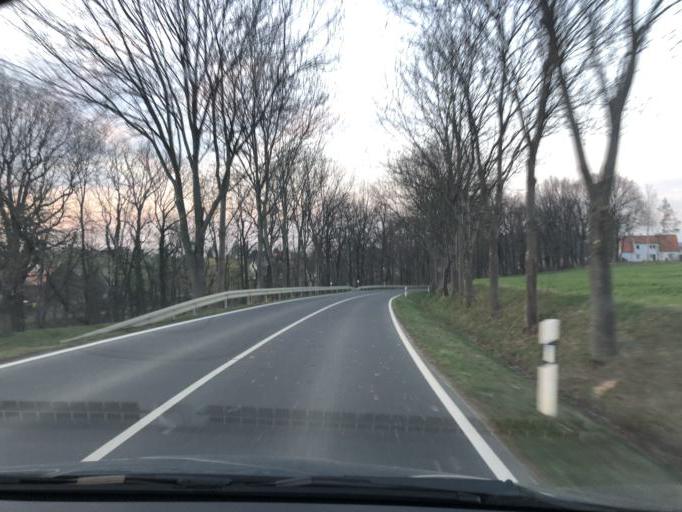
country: DE
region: Saxony
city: Elstra
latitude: 51.2317
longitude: 14.1294
